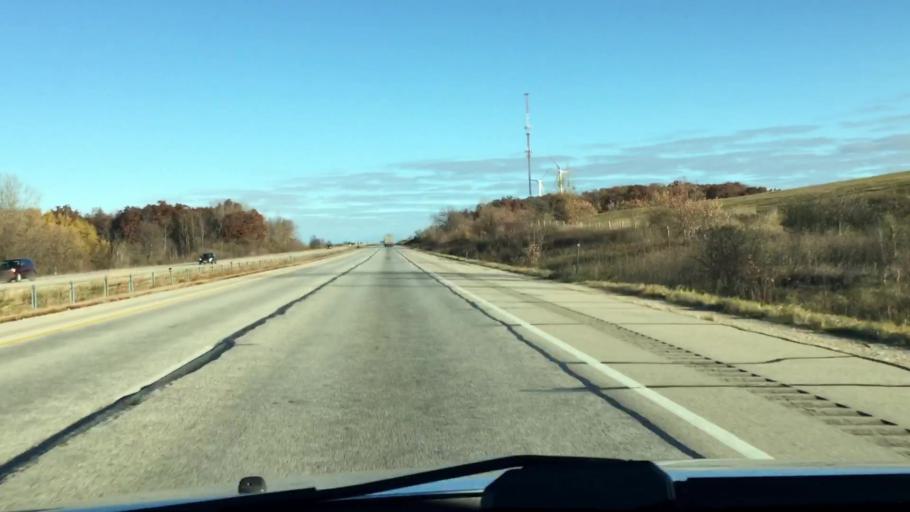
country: US
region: Wisconsin
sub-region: Dodge County
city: Lomira
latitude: 43.6483
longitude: -88.4414
